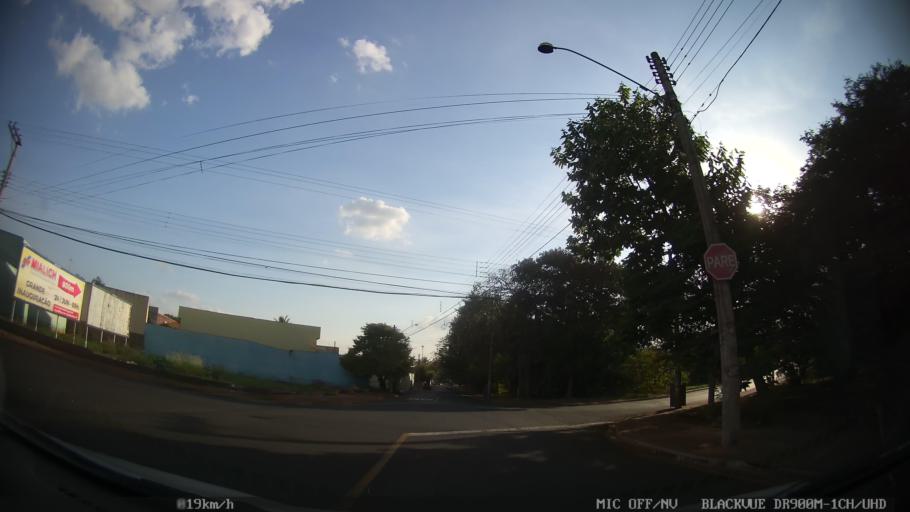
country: BR
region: Sao Paulo
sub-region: Ribeirao Preto
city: Ribeirao Preto
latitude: -21.1455
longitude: -47.8324
